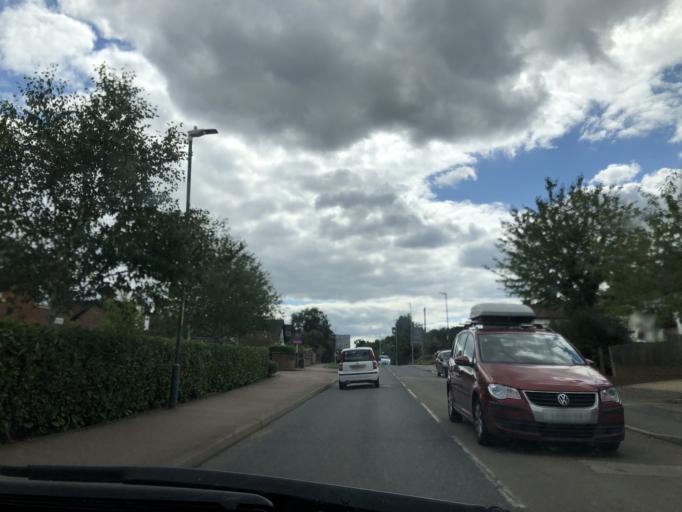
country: GB
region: England
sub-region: Kent
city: Edenbridge
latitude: 51.2049
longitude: 0.0622
